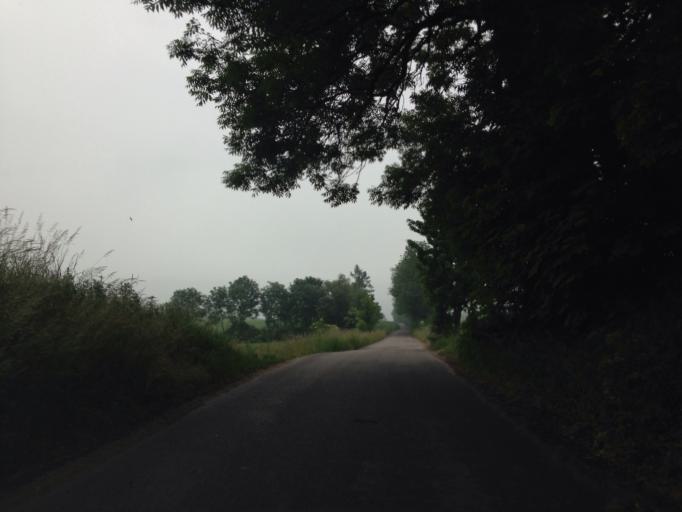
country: PL
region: Kujawsko-Pomorskie
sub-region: Powiat brodnicki
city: Jablonowo Pomorskie
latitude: 53.4414
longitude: 19.1903
